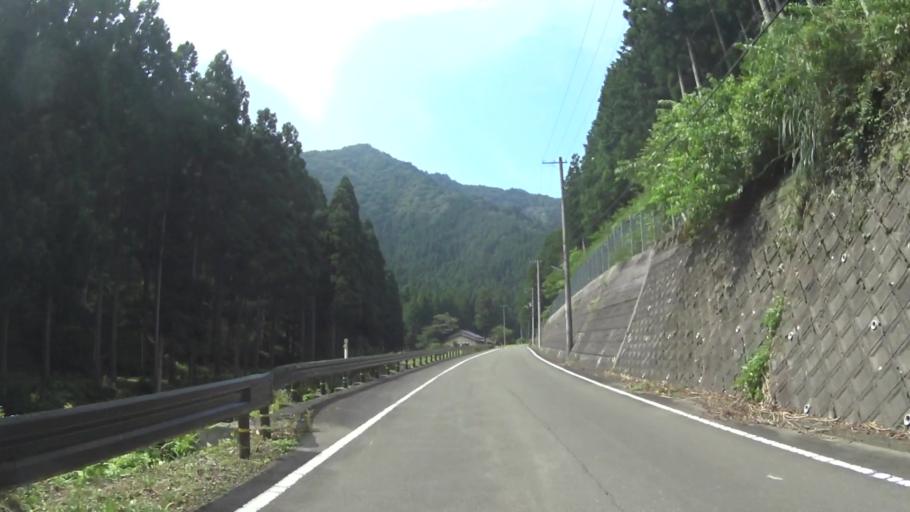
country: JP
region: Fukui
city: Obama
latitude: 35.3239
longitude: 135.6443
